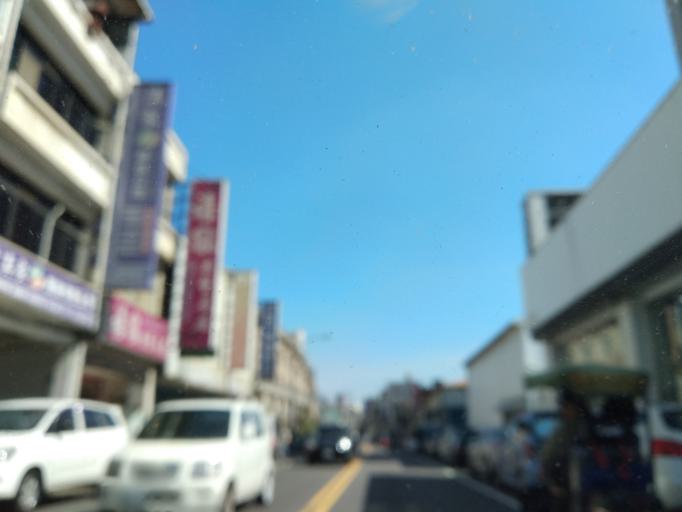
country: TW
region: Taiwan
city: Taoyuan City
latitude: 24.9473
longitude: 121.2073
